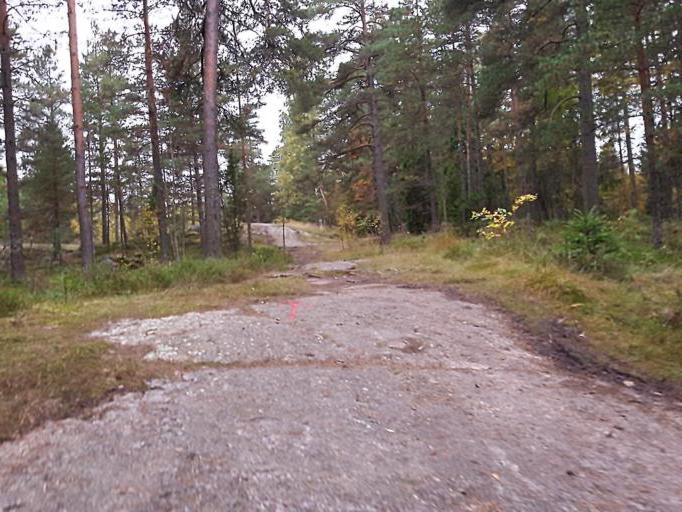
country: FI
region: Uusimaa
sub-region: Helsinki
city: Helsinki
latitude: 60.2593
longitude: 24.9053
